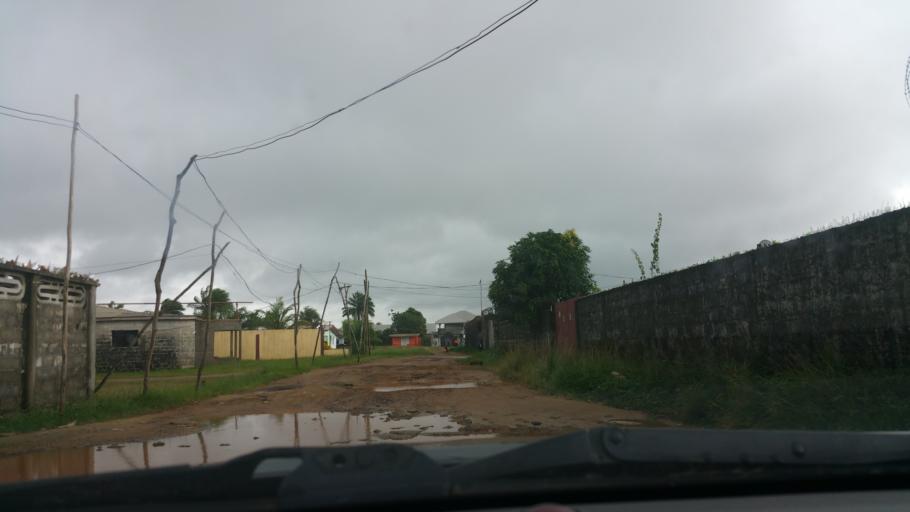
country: LR
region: Montserrado
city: Monrovia
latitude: 6.2370
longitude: -10.6685
